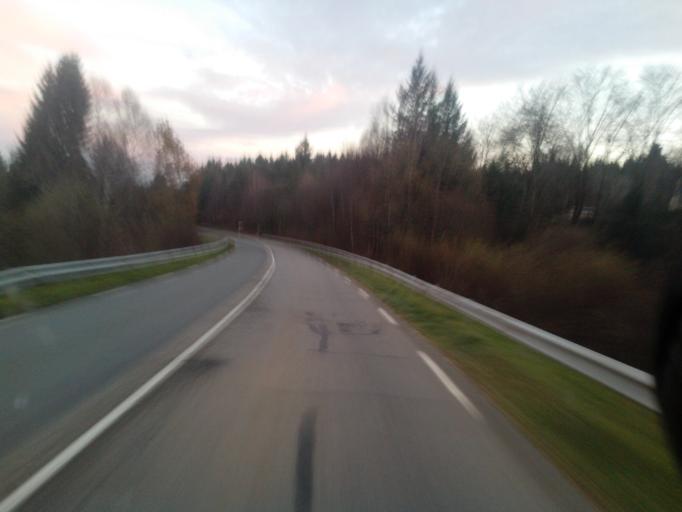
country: FR
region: Limousin
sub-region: Departement de la Correze
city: Meymac
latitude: 45.5162
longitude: 2.1763
